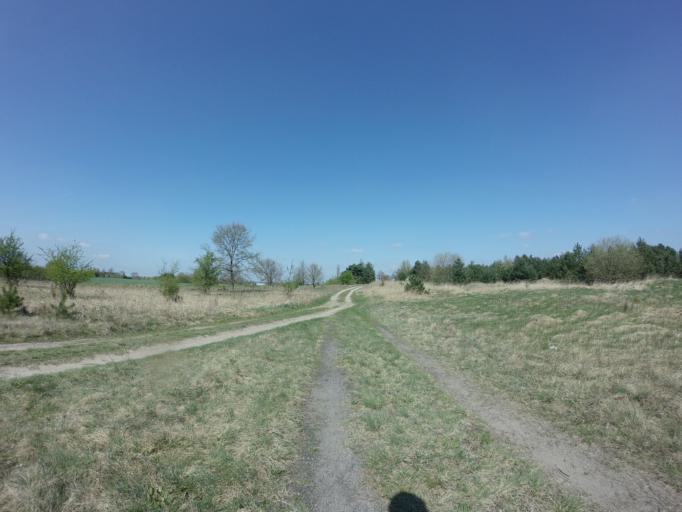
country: PL
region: West Pomeranian Voivodeship
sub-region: Powiat choszczenski
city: Choszczno
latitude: 53.1609
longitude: 15.4559
